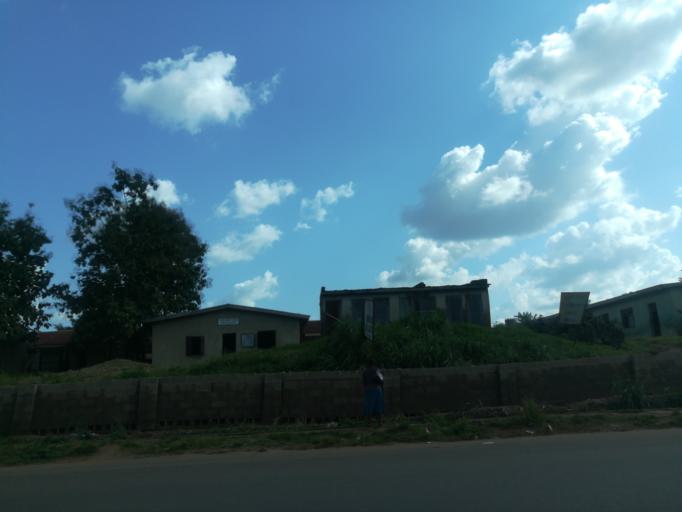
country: NG
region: Oyo
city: Egbeda
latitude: 7.4241
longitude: 3.9845
